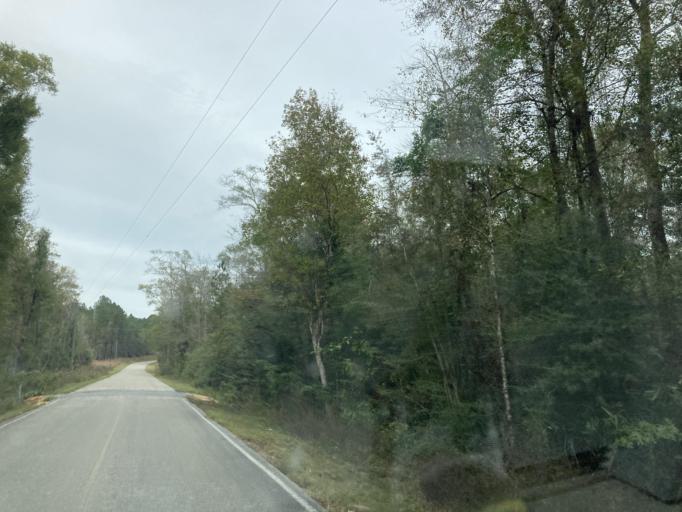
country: US
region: Mississippi
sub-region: Lamar County
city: Lumberton
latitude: 31.0611
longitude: -89.4336
